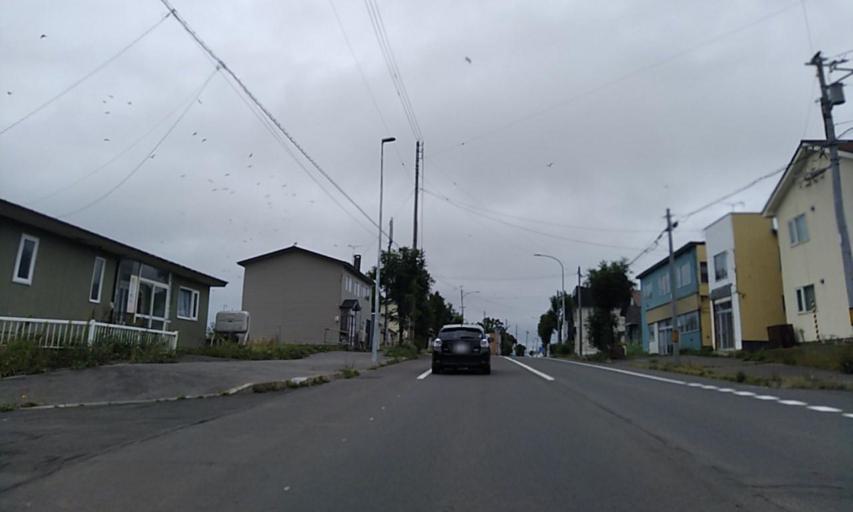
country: JP
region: Hokkaido
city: Nemuro
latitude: 43.3344
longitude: 145.5780
